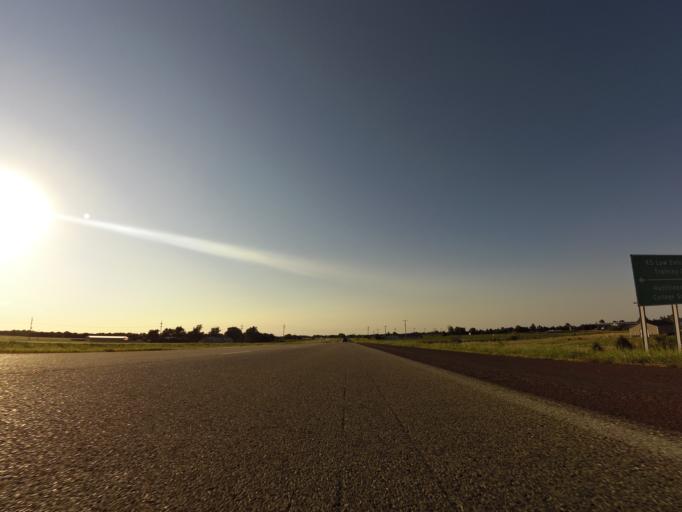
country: US
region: Kansas
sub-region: Reno County
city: South Hutchinson
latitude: 37.9424
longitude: -97.8824
